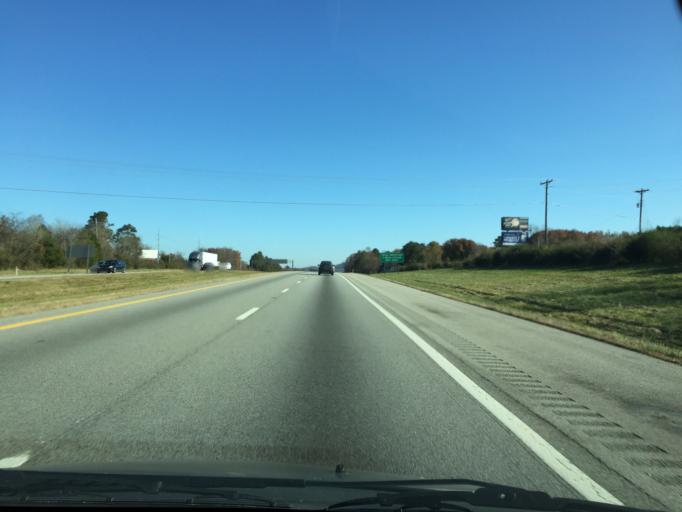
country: US
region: Tennessee
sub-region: Bradley County
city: Cleveland
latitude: 35.1768
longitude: -84.9161
